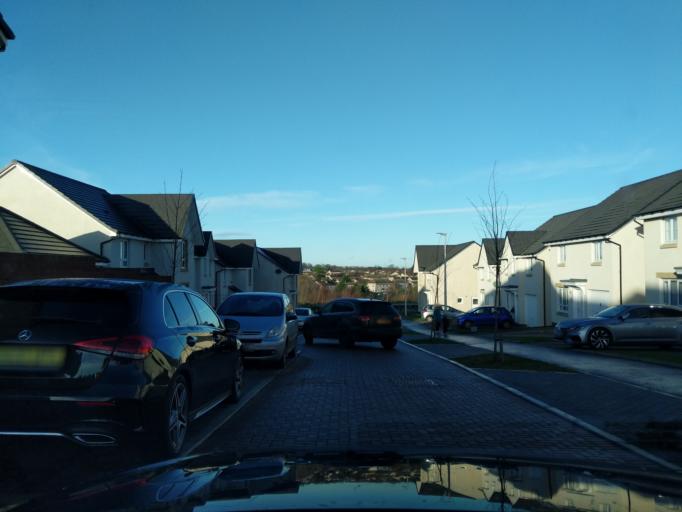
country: GB
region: Scotland
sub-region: Midlothian
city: Loanhead
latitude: 55.8946
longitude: -3.1528
